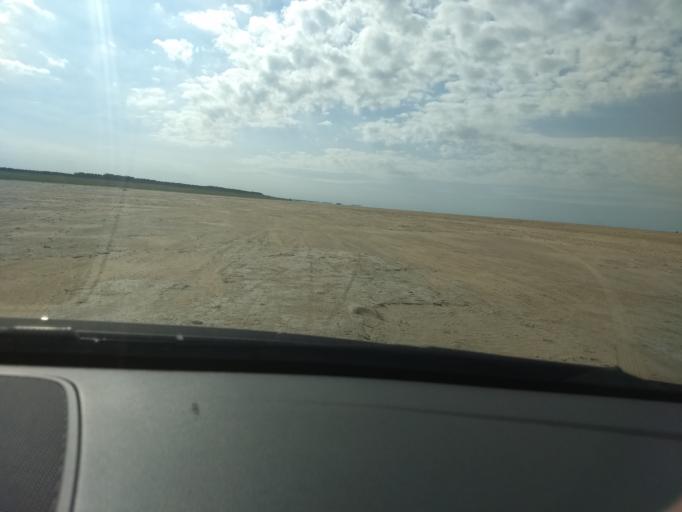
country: DE
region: Schleswig-Holstein
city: List
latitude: 55.0906
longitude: 8.4986
